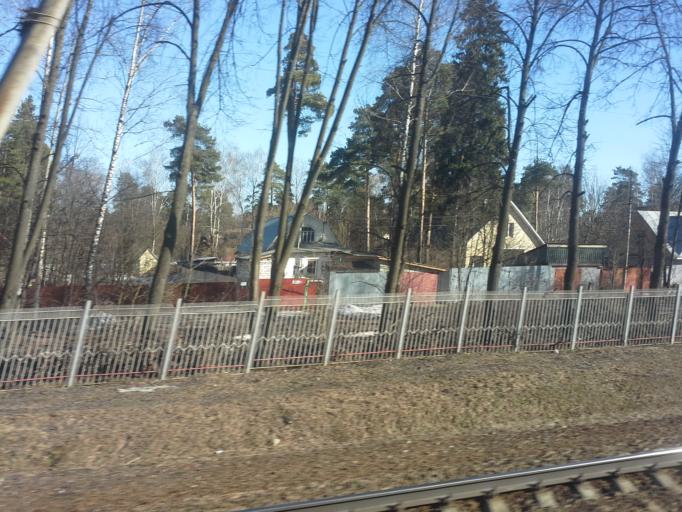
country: RU
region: Moskovskaya
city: Mamontovka
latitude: 55.9864
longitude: 37.8242
